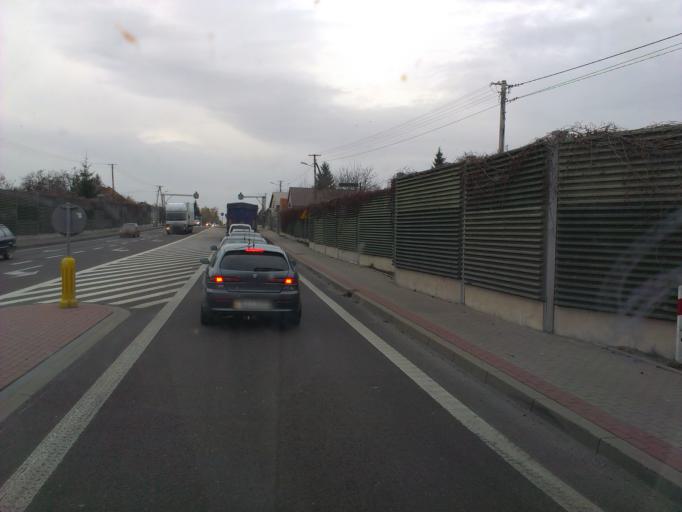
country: PL
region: Subcarpathian Voivodeship
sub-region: Powiat rzeszowski
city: Krasne
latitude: 50.0415
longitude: 22.0951
